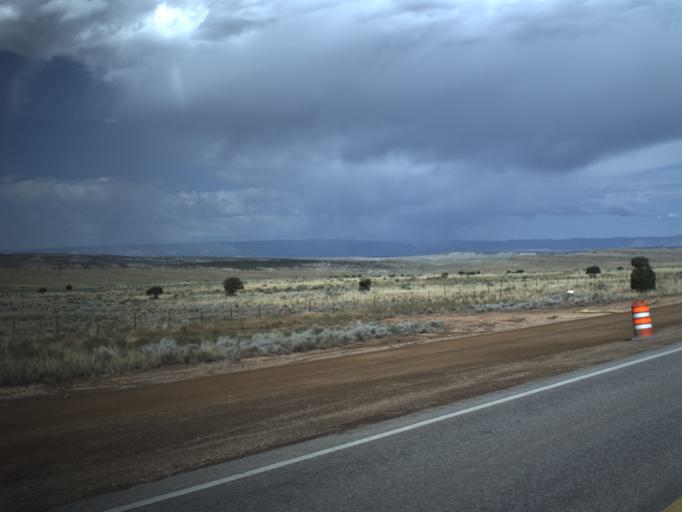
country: US
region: Utah
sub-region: Carbon County
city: East Carbon City
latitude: 39.4246
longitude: -110.4453
